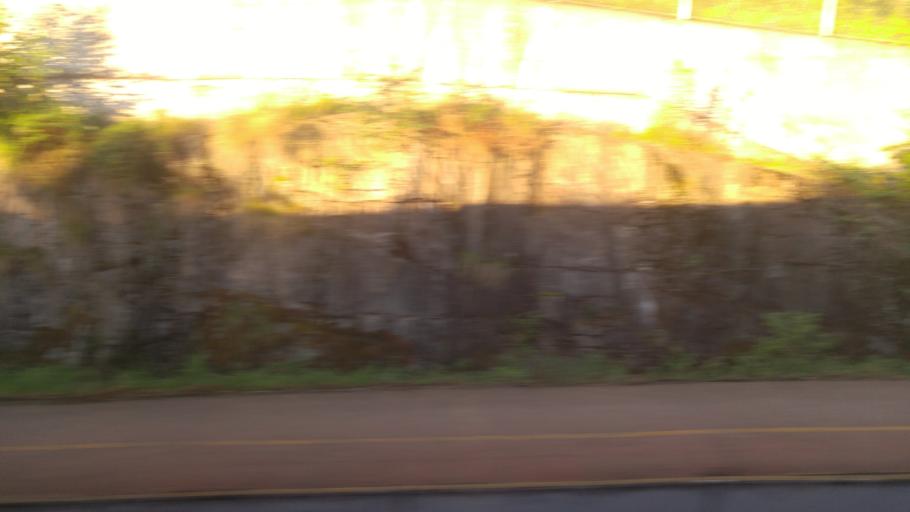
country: NO
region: Akershus
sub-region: Skedsmo
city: Lillestrom
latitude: 59.9559
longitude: 11.0177
